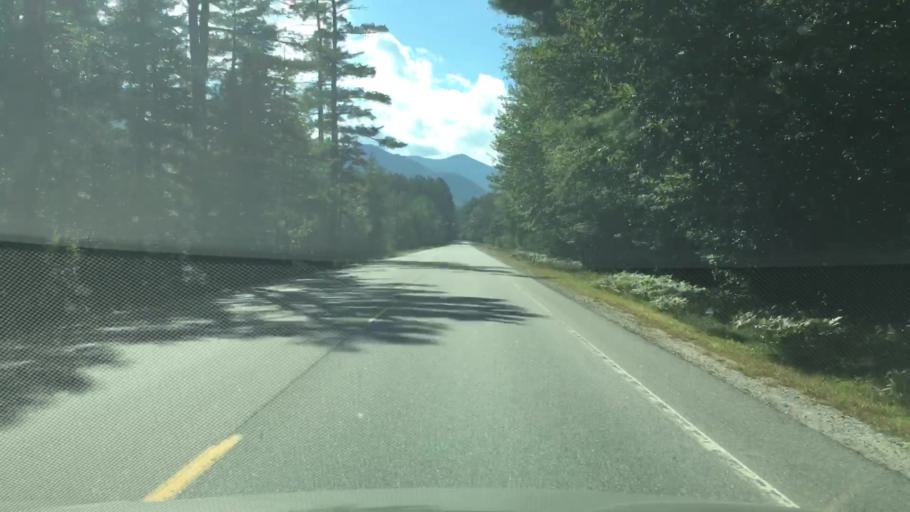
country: US
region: New Hampshire
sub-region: Carroll County
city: Tamworth
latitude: 43.9974
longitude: -71.3597
